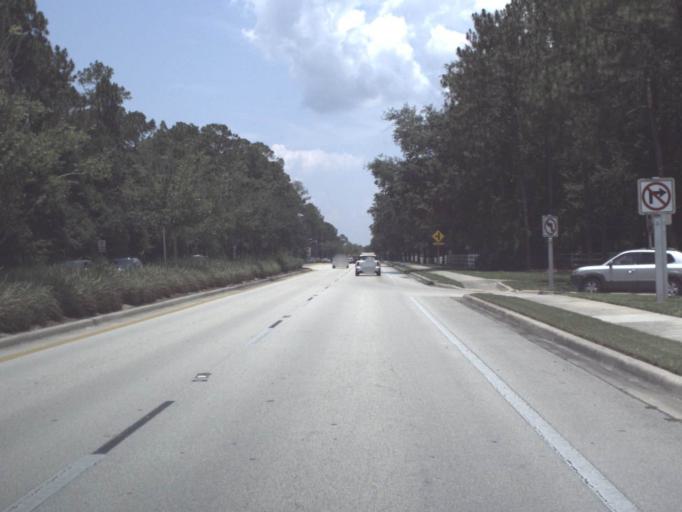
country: US
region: Florida
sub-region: Saint Johns County
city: Fruit Cove
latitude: 30.1088
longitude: -81.6265
